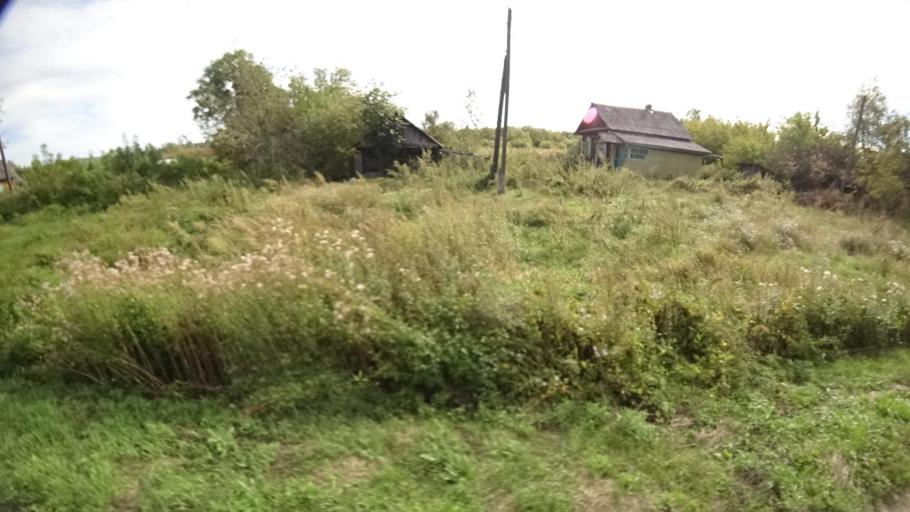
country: RU
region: Primorskiy
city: Dostoyevka
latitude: 44.3279
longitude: 133.4930
